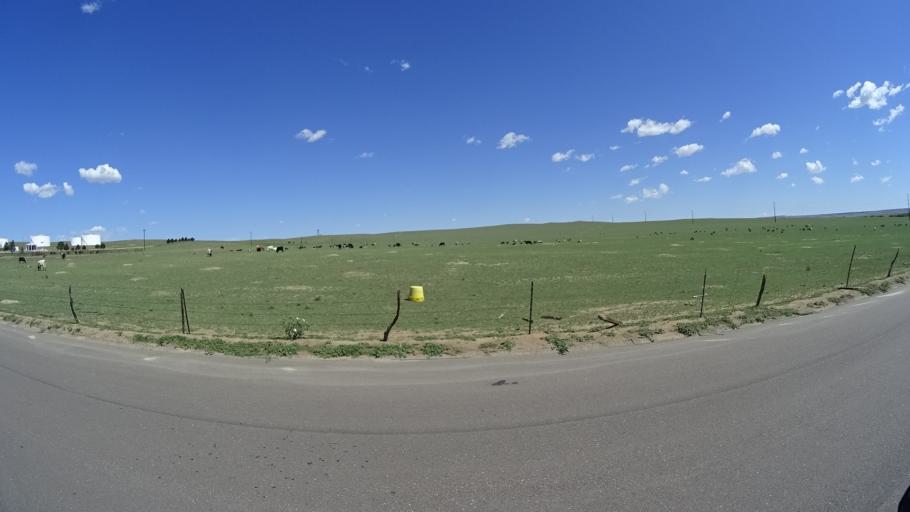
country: US
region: Colorado
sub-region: El Paso County
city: Security-Widefield
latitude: 38.7811
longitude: -104.6717
